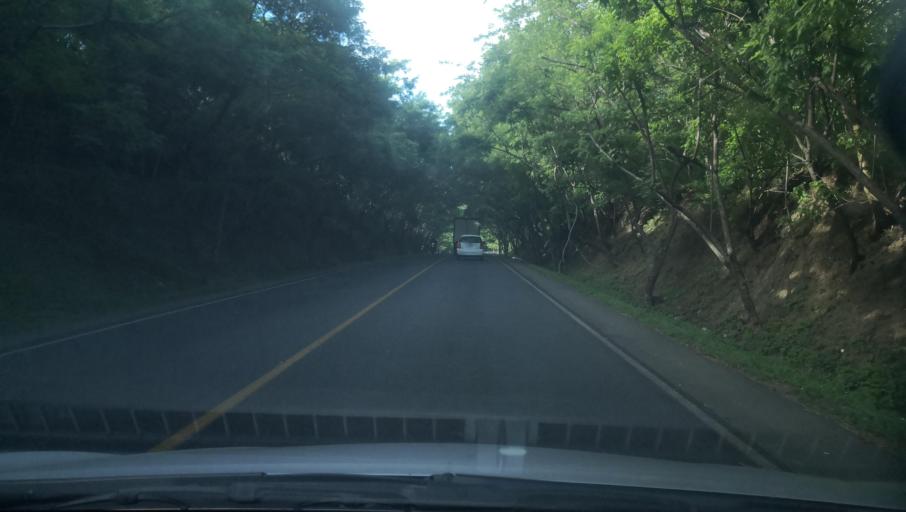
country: NI
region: Madriz
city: Totogalpa
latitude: 13.5658
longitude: -86.4853
